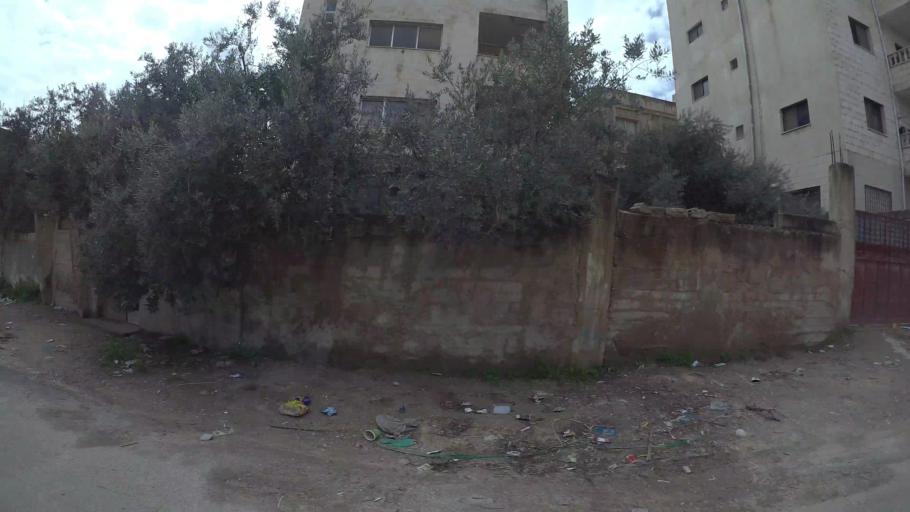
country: JO
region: Amman
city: Al Jubayhah
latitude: 32.0602
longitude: 35.8285
